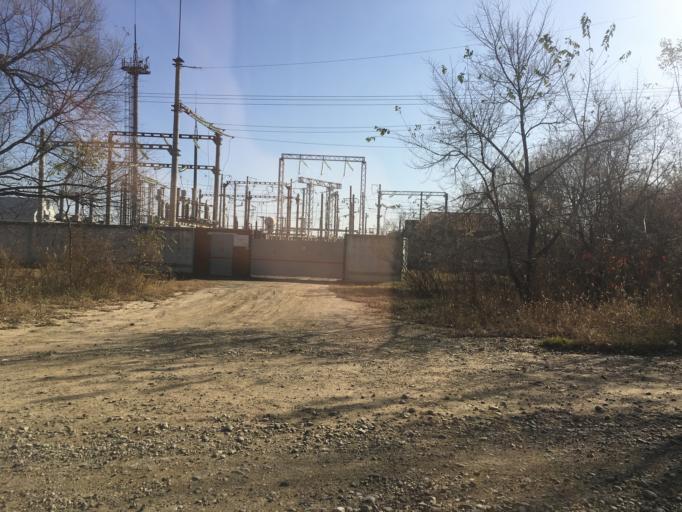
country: RU
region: Primorskiy
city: Dal'nerechensk
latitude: 45.9284
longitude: 133.7092
